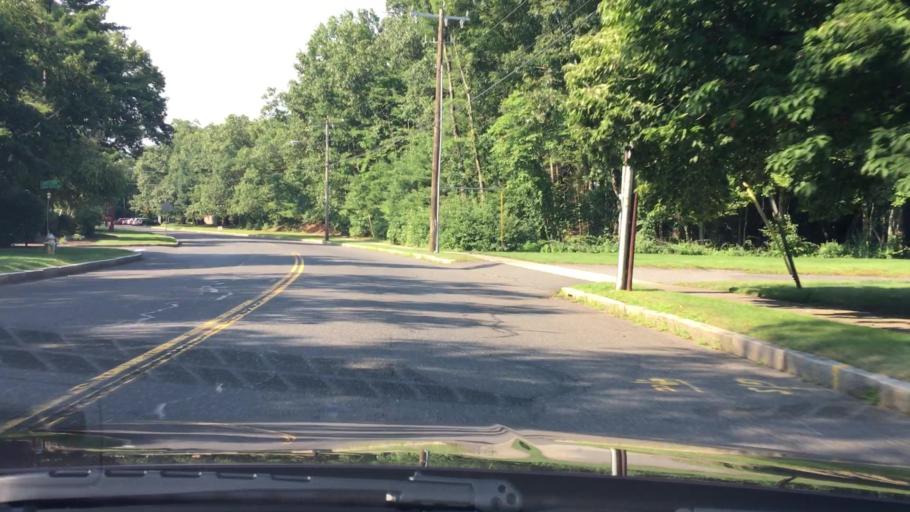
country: US
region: Massachusetts
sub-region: Hampden County
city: Longmeadow
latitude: 42.0696
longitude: -72.5551
